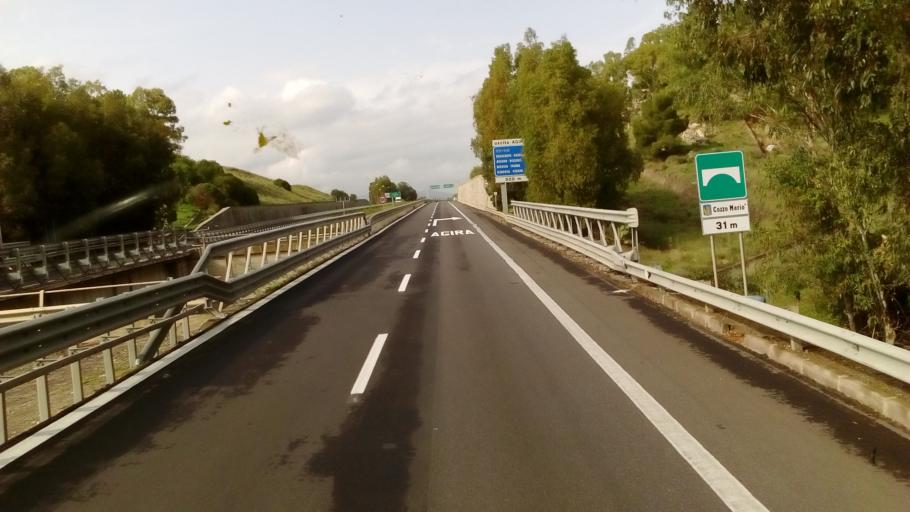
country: IT
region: Sicily
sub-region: Catania
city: Raddusa
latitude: 37.5440
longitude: 14.5429
